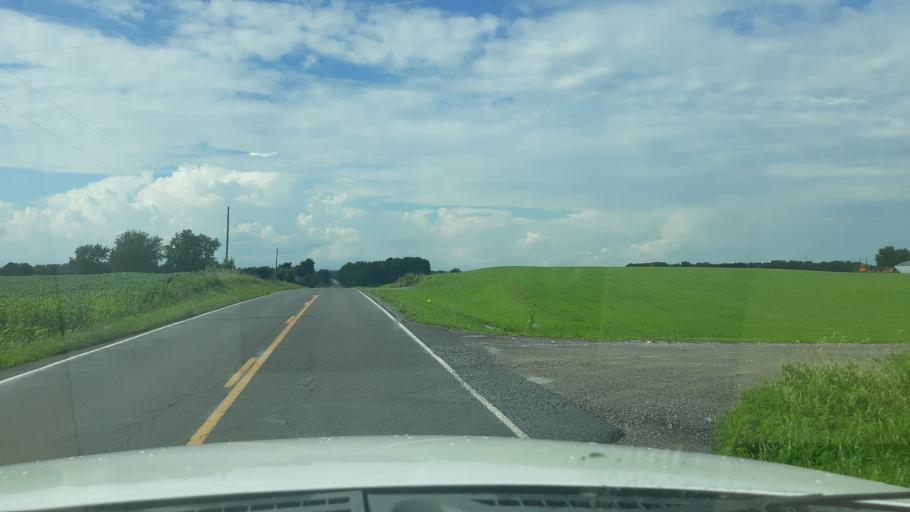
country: US
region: Illinois
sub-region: Saline County
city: Eldorado
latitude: 37.8434
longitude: -88.5304
